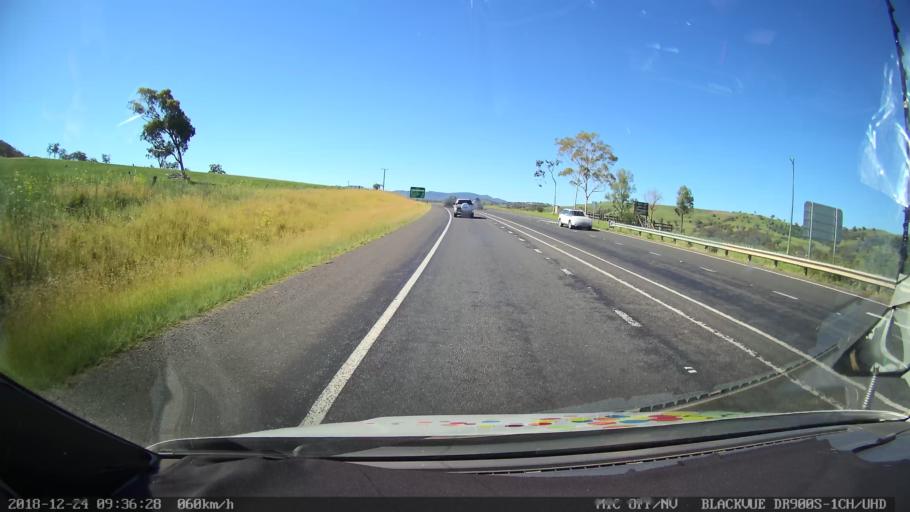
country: AU
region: New South Wales
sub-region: Liverpool Plains
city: Quirindi
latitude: -31.6381
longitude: 150.7220
